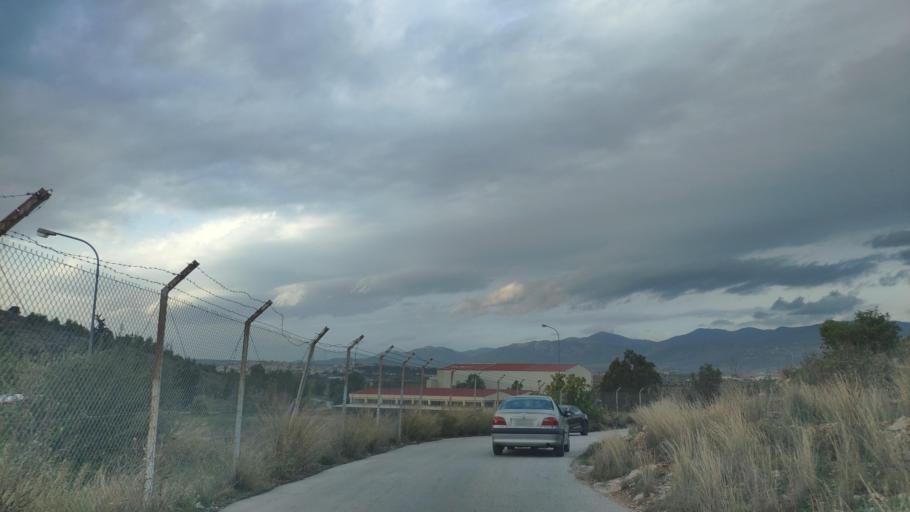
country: GR
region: Attica
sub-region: Nomarchia Dytikis Attikis
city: Megara
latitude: 37.9771
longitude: 23.3711
